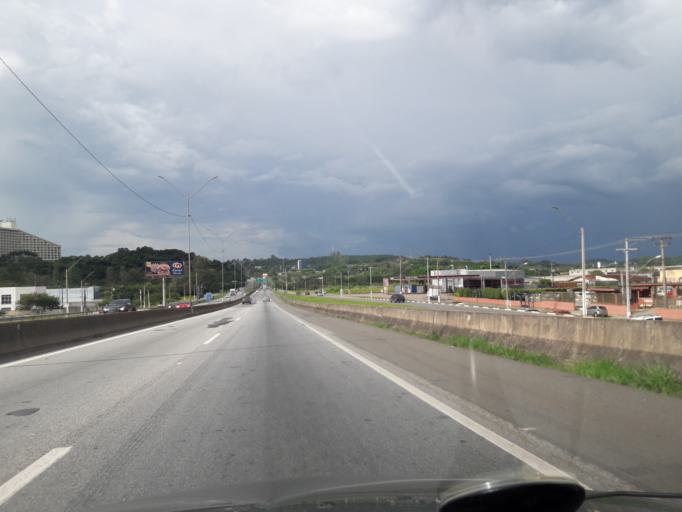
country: BR
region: Sao Paulo
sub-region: Atibaia
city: Atibaia
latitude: -23.1146
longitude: -46.5721
